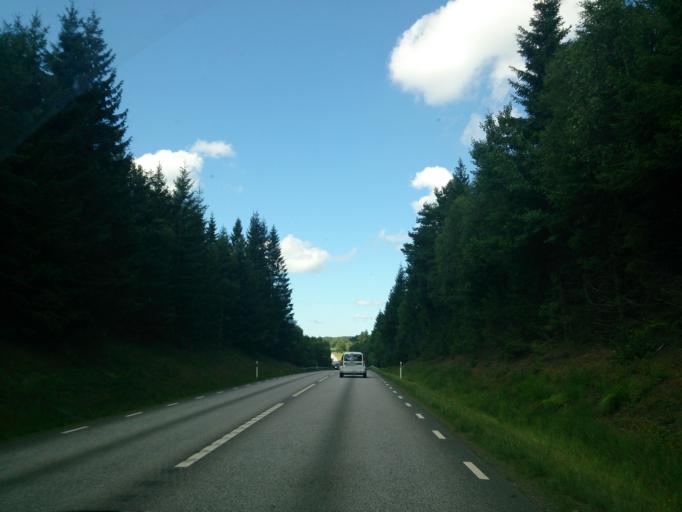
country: SE
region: Halland
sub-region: Halmstads Kommun
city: Getinge
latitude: 57.0985
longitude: 12.8041
